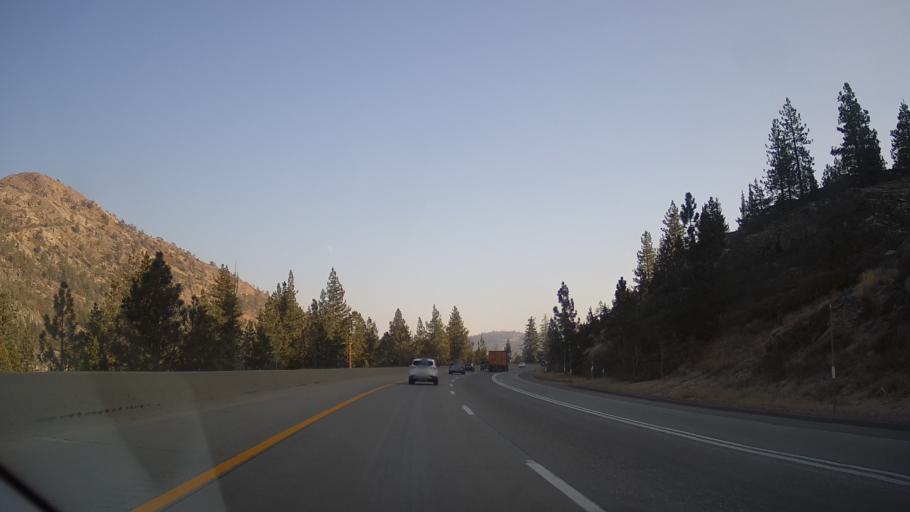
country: US
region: California
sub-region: Sierra County
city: Downieville
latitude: 39.3266
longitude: -120.5733
